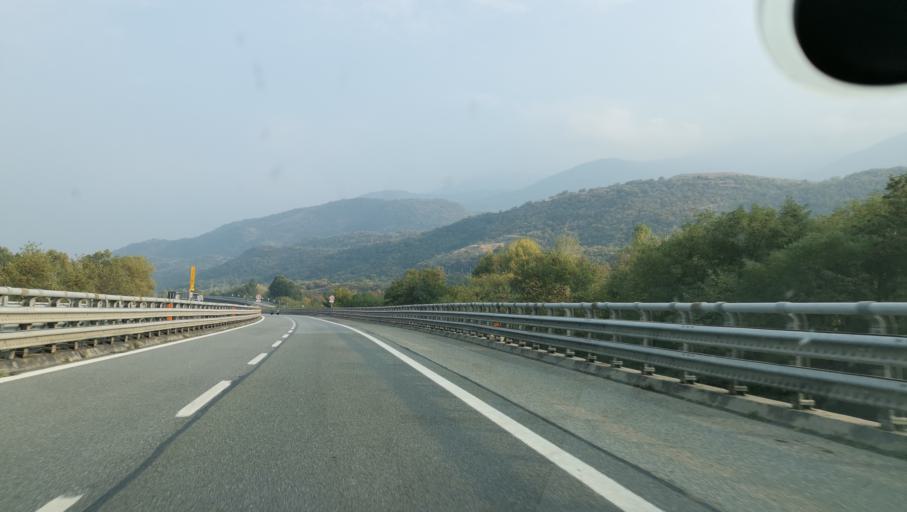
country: IT
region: Piedmont
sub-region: Provincia di Torino
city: Mattie
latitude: 45.1341
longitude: 7.0966
